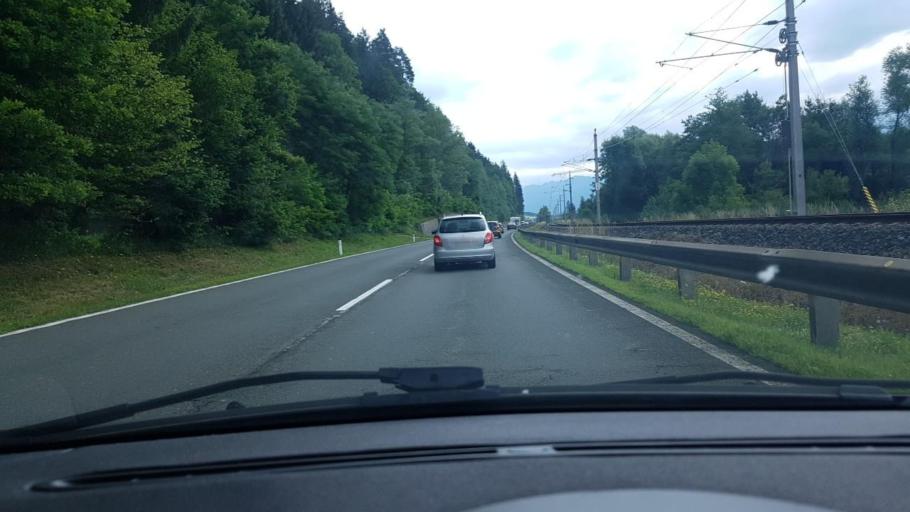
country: AT
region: Carinthia
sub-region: Politischer Bezirk Villach Land
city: Feistritz an der Gail
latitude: 46.5970
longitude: 13.5915
